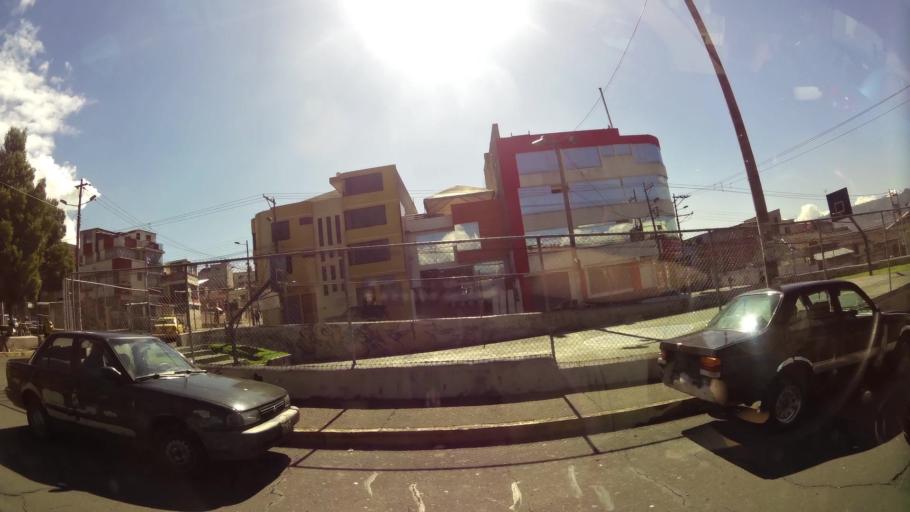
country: EC
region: Pichincha
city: Quito
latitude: -0.2371
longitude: -78.5296
